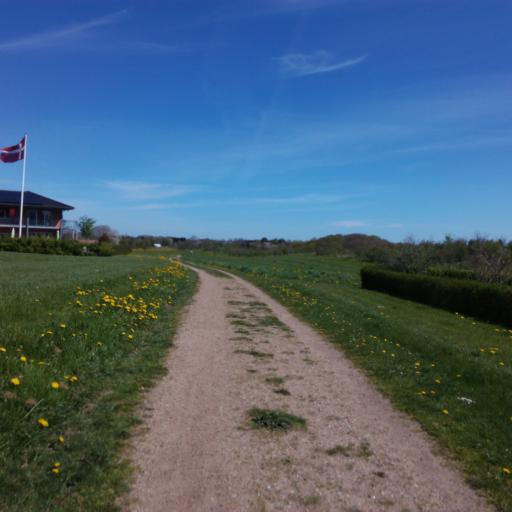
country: DK
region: South Denmark
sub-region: Vejle Kommune
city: Borkop
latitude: 55.6299
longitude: 9.6602
